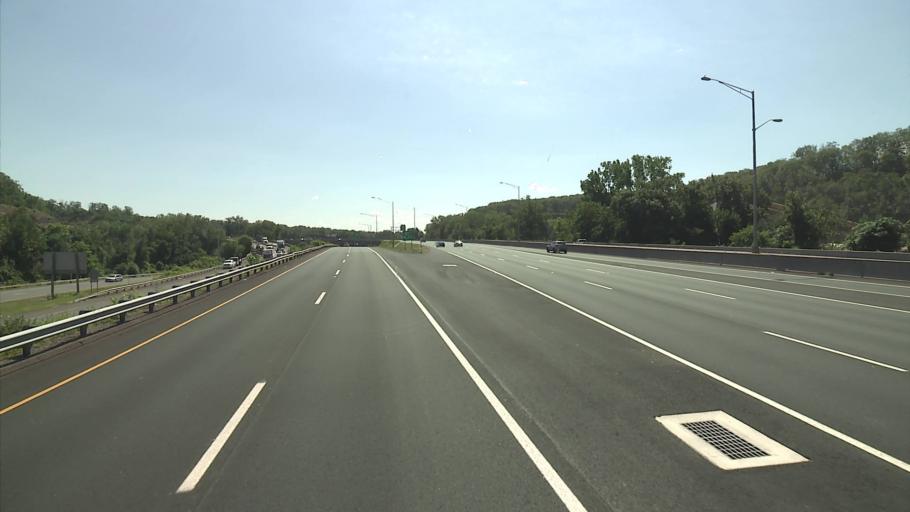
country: US
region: Connecticut
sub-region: Hartford County
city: Plainville
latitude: 41.6686
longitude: -72.8294
